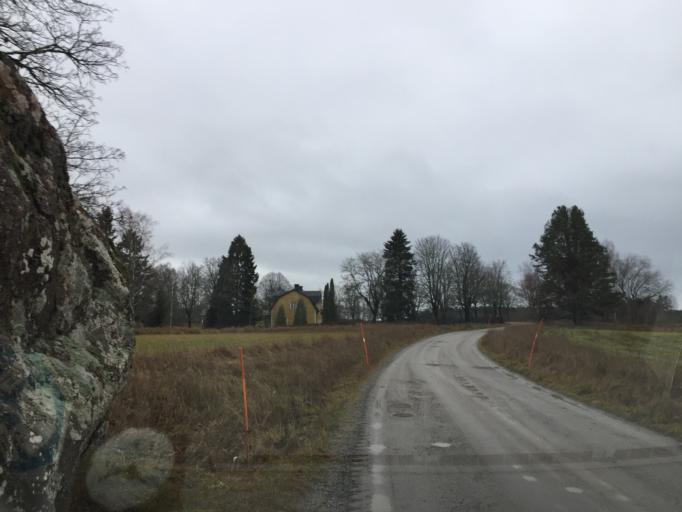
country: SE
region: Stockholm
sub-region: Nynashamns Kommun
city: Osmo
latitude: 59.0444
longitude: 17.8919
